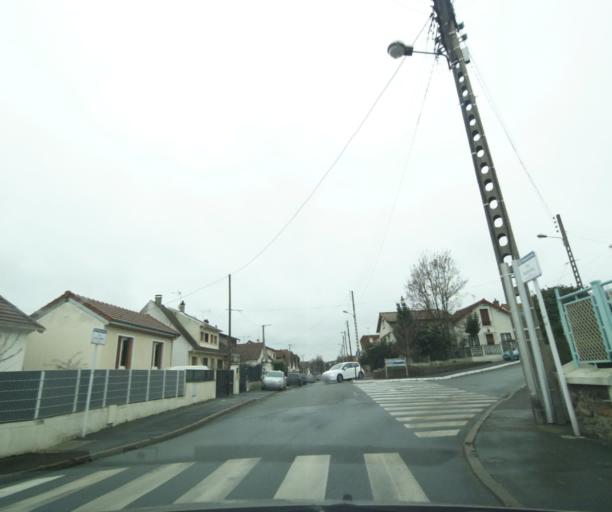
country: FR
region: Ile-de-France
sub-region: Departement du Val-de-Marne
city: Villeneuve-le-Roi
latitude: 48.7343
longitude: 2.4118
